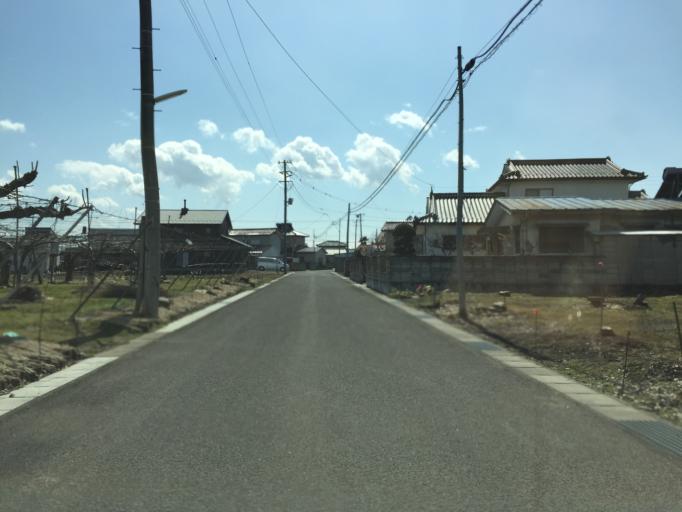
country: JP
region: Fukushima
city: Fukushima-shi
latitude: 37.7986
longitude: 140.4206
